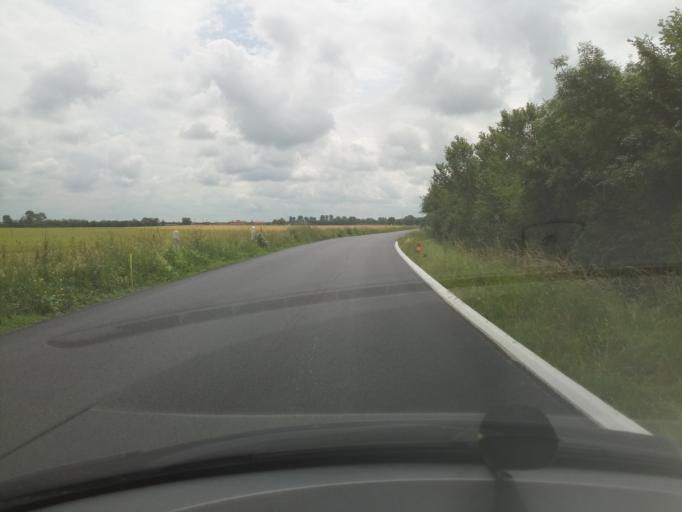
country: FR
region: Poitou-Charentes
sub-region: Departement de la Charente-Maritime
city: Saint-Jean-de-Liversay
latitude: 46.2743
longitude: -0.9037
